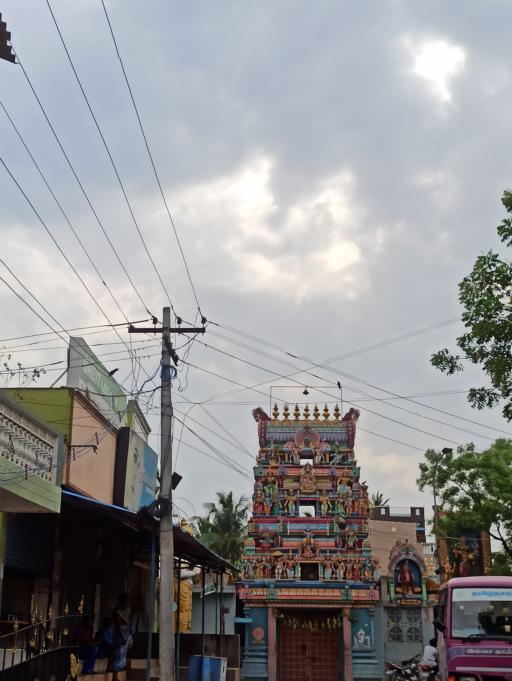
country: IN
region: Tamil Nadu
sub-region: Thiruvallur
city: Chinnasekkadu
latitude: 13.1677
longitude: 80.2435
